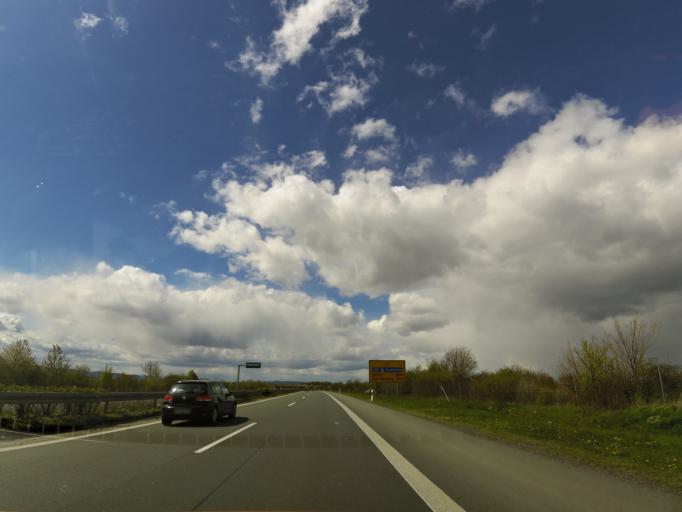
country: DE
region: Saxony-Anhalt
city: Stapelburg
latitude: 51.9354
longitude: 10.6337
